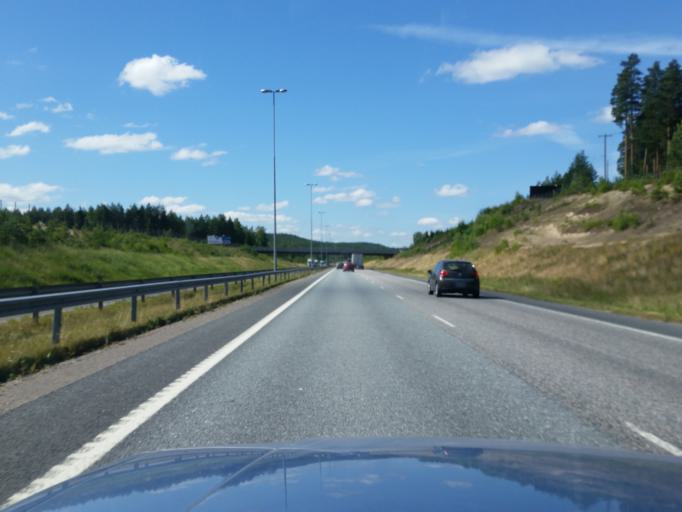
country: FI
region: Uusimaa
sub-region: Helsinki
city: Lohja
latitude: 60.2941
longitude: 24.1746
